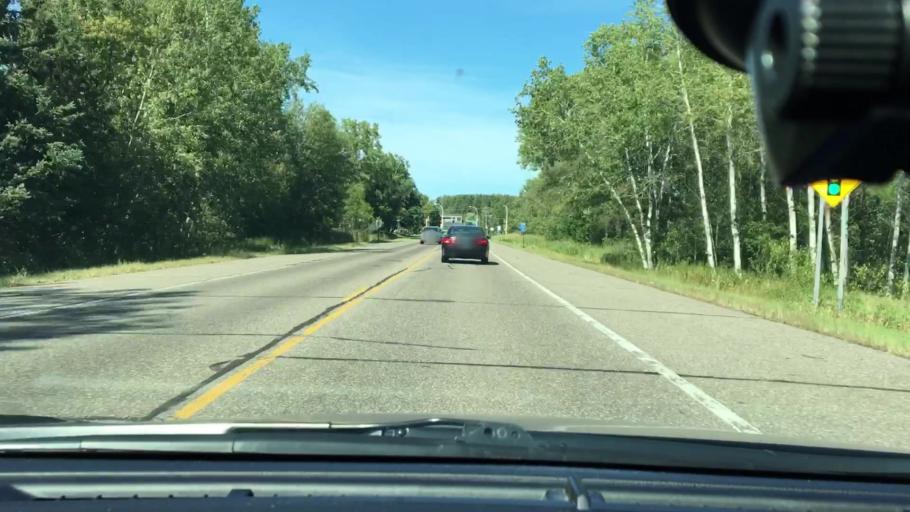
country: US
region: Minnesota
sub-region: Washington County
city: Mahtomedi
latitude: 45.0541
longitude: -92.9475
